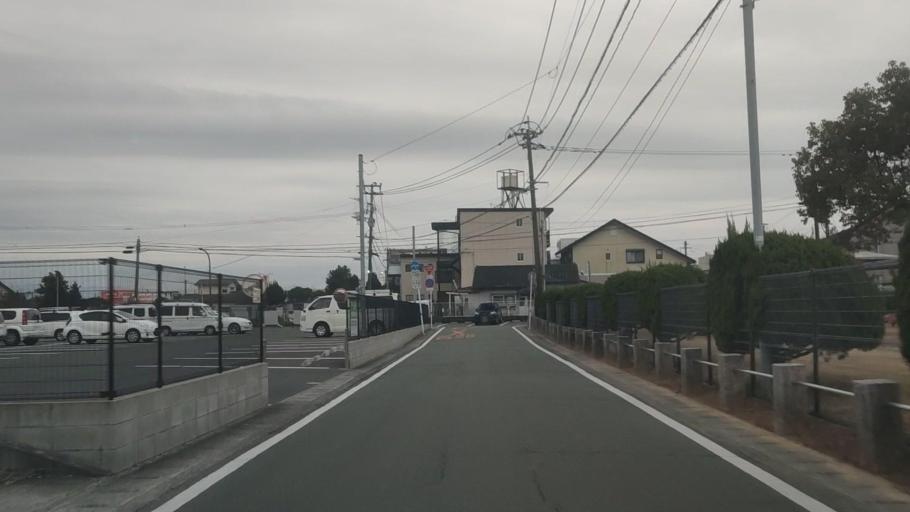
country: JP
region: Kumamoto
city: Kumamoto
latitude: 32.7663
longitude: 130.7099
